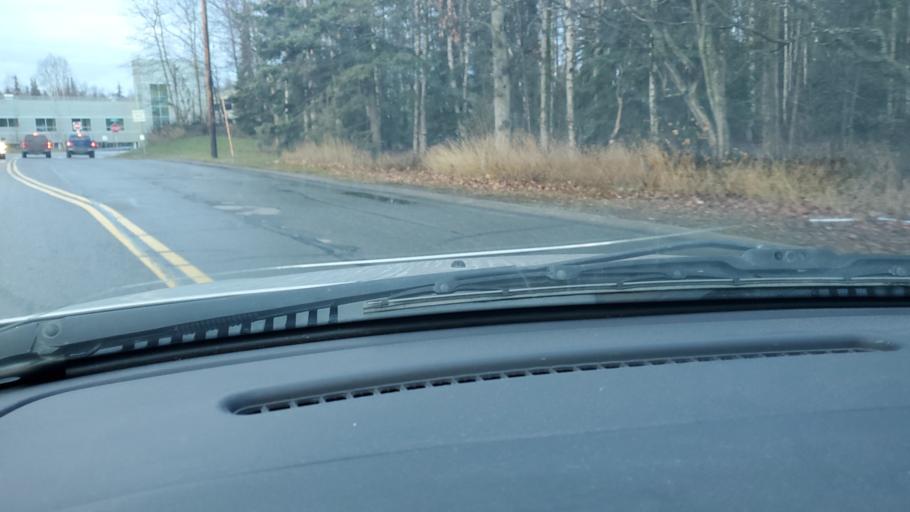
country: US
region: Alaska
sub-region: Anchorage Municipality
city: Anchorage
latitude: 61.1915
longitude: -149.8219
